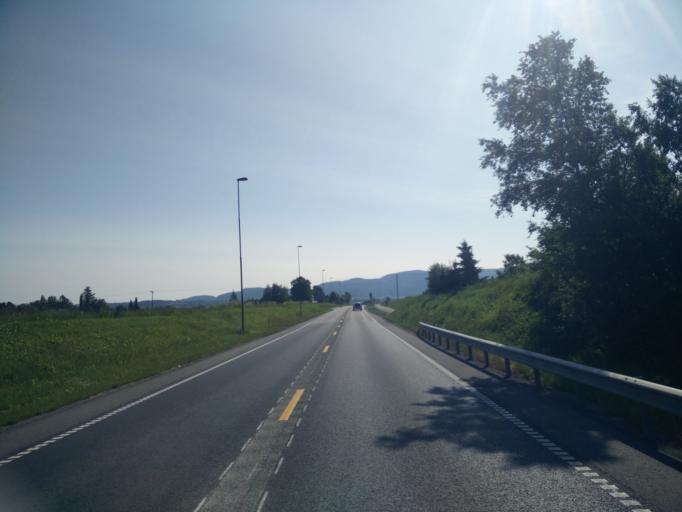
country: NO
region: Sor-Trondelag
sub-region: Melhus
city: Melhus
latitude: 63.3231
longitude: 10.2489
